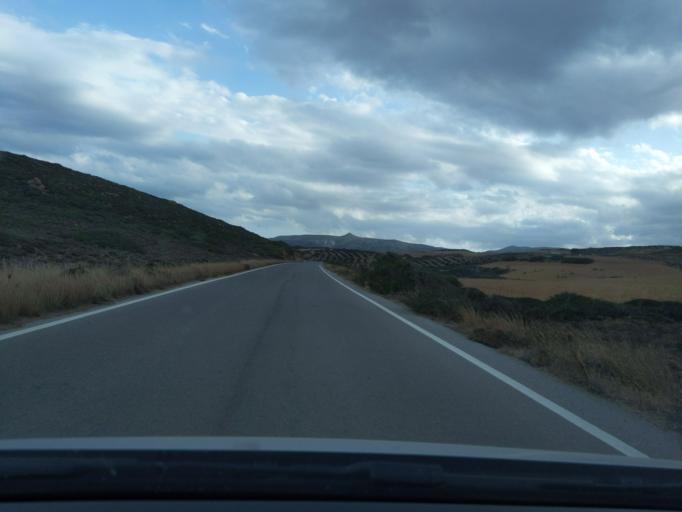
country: GR
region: Crete
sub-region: Nomos Lasithiou
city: Palekastro
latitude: 35.2339
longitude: 26.2522
